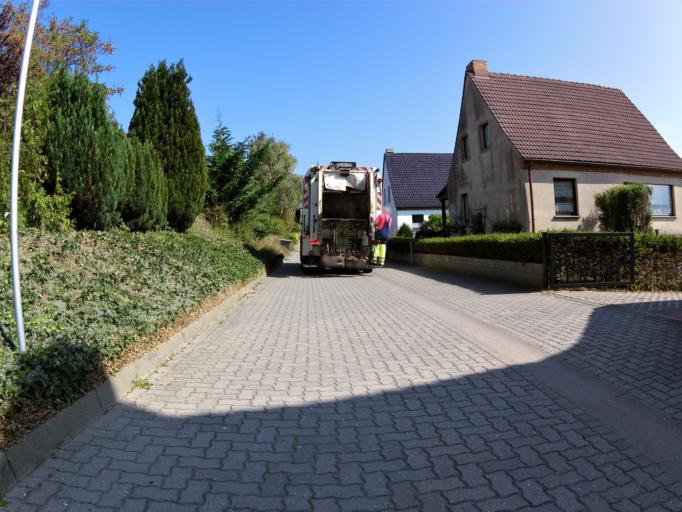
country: DE
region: Mecklenburg-Vorpommern
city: Loddin
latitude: 54.0108
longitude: 14.0448
